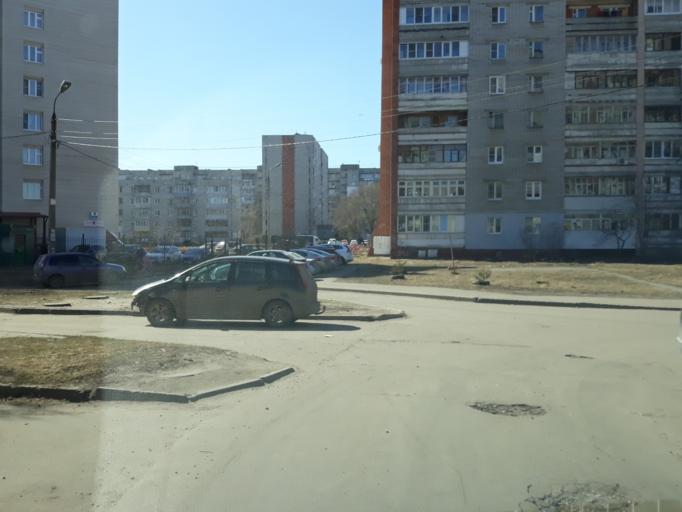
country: RU
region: Jaroslavl
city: Yaroslavl
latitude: 57.6560
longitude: 39.9479
